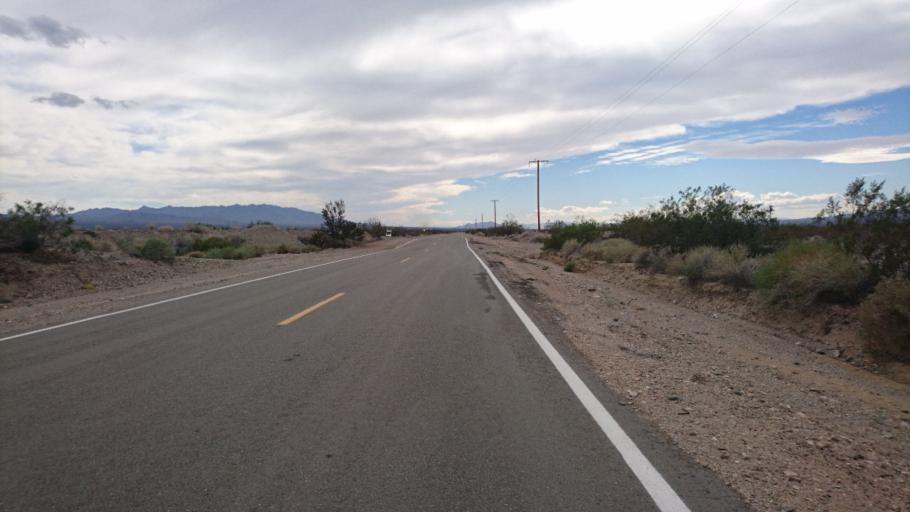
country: US
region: California
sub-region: San Bernardino County
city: Needles
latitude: 34.7843
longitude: -115.2049
